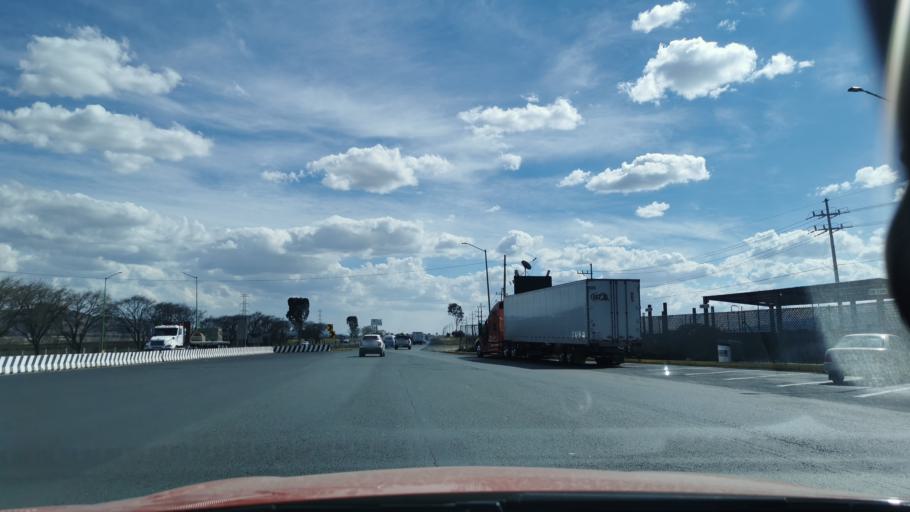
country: MX
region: Mexico
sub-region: Atlacomulco
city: Tecoac (Santa Maria Nativitas)
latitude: 19.7621
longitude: -99.8554
